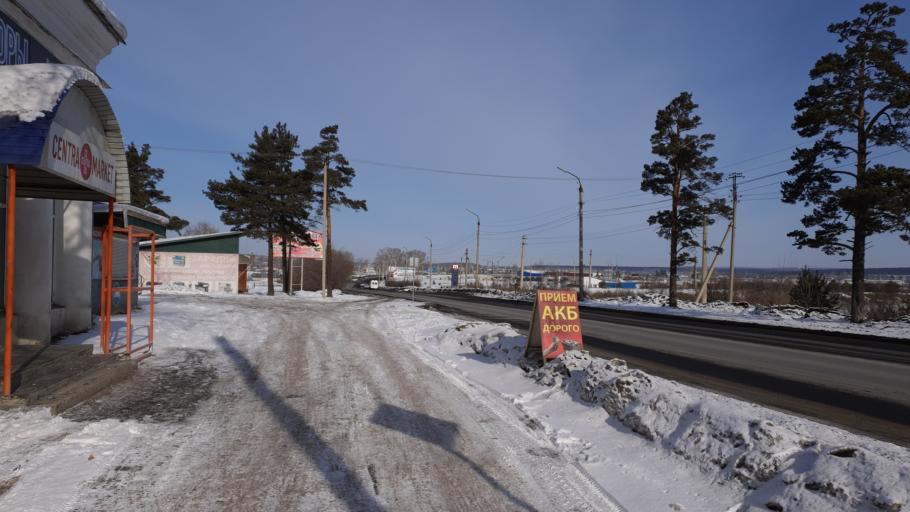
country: RU
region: Irkutsk
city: Tulun
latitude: 54.5416
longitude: 100.5933
